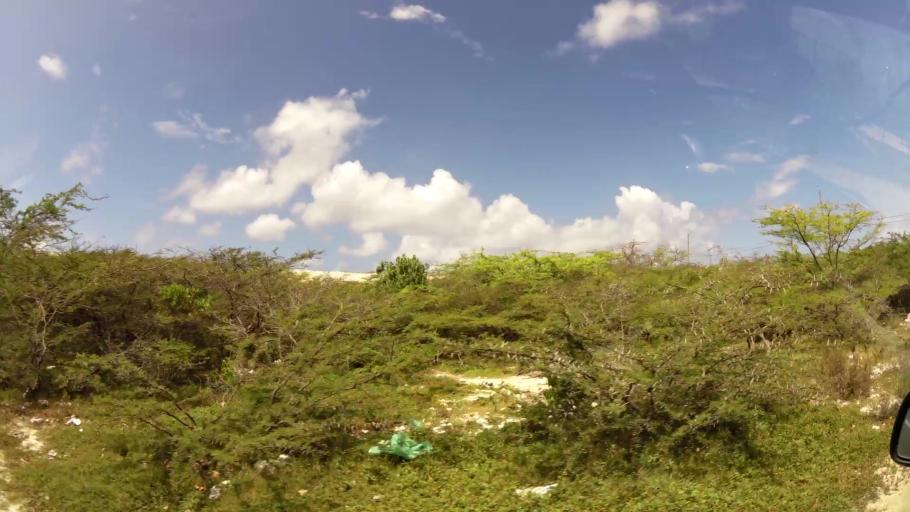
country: TC
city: Cockburn Town
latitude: 21.4906
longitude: -71.1425
